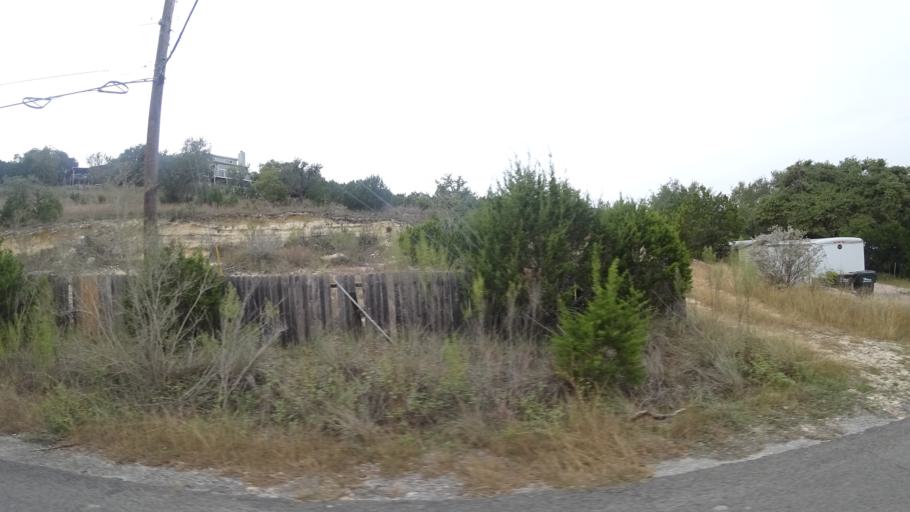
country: US
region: Texas
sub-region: Travis County
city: Hudson Bend
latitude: 30.3749
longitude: -97.9161
